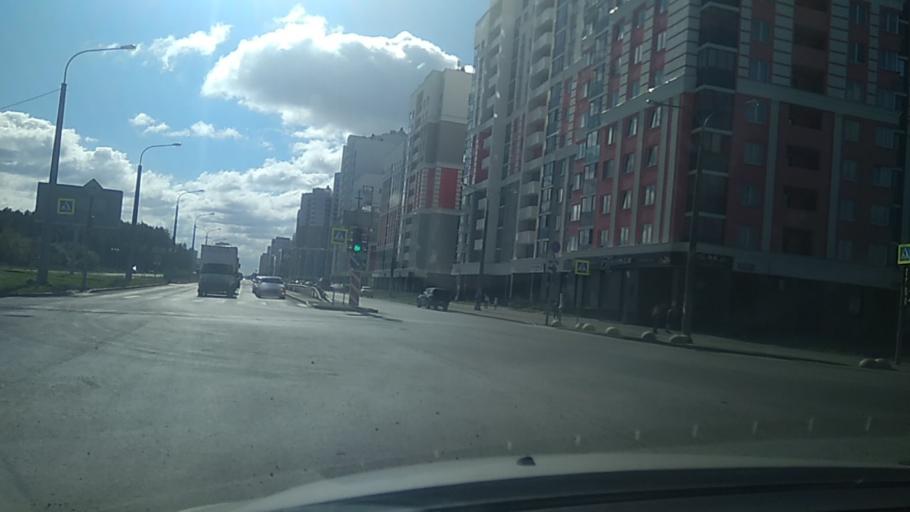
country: RU
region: Sverdlovsk
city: Shirokaya Rechka
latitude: 56.7980
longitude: 60.5129
